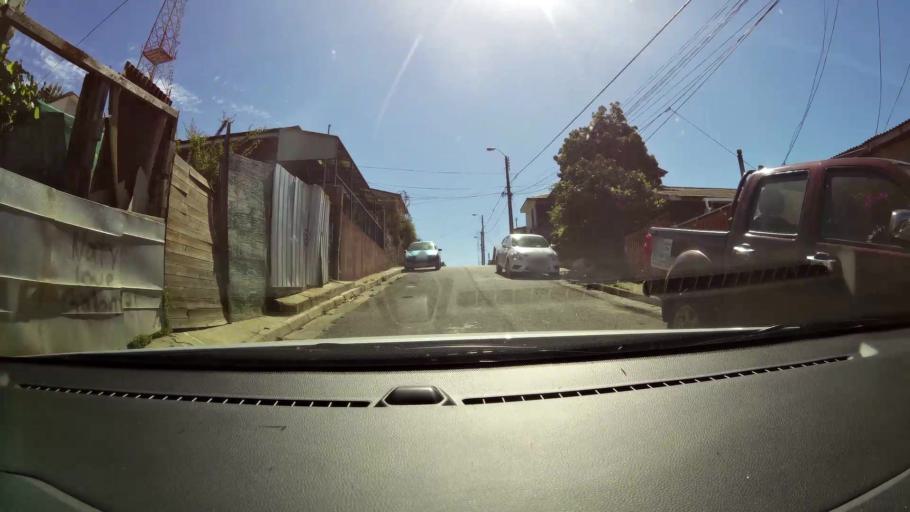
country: CL
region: Valparaiso
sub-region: Provincia de Valparaiso
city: Vina del Mar
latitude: -33.0424
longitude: -71.5662
